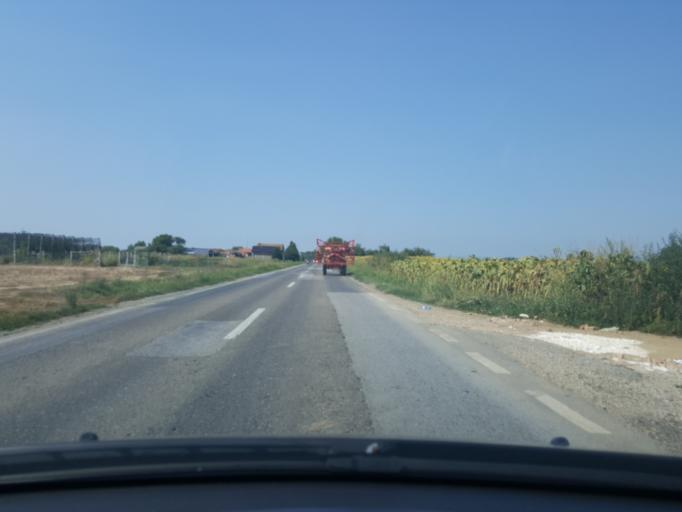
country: RS
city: Hrtkovci
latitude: 44.8647
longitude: 19.7714
